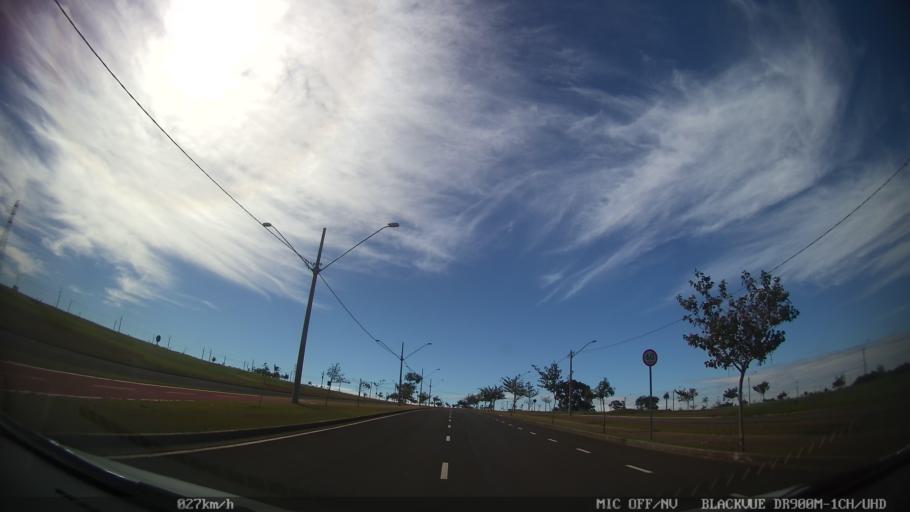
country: BR
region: Sao Paulo
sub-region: Sao Jose Do Rio Preto
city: Sao Jose do Rio Preto
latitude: -20.8555
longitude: -49.3763
